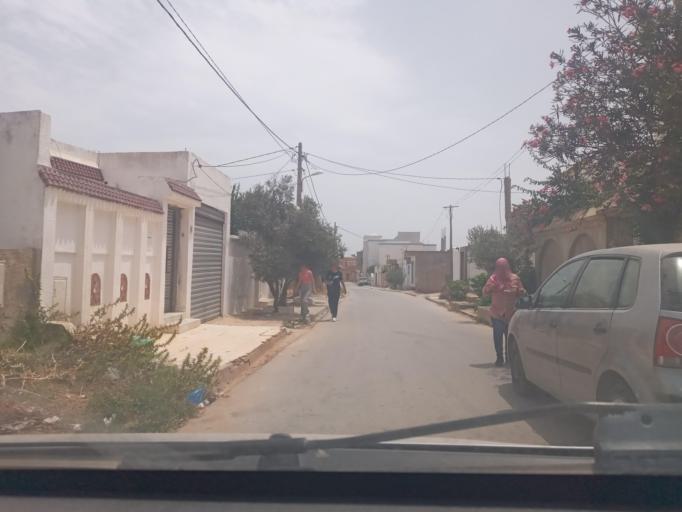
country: TN
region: Nabul
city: El Haouaria
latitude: 37.0531
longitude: 11.0105
